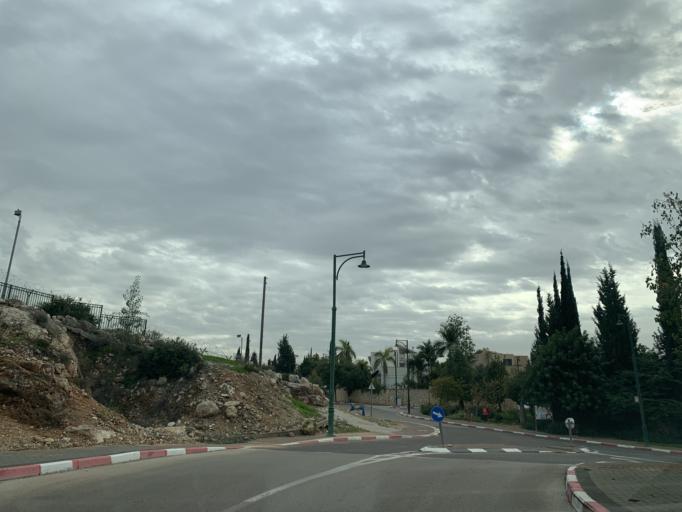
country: IL
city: Nirit
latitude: 32.1480
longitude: 34.9873
